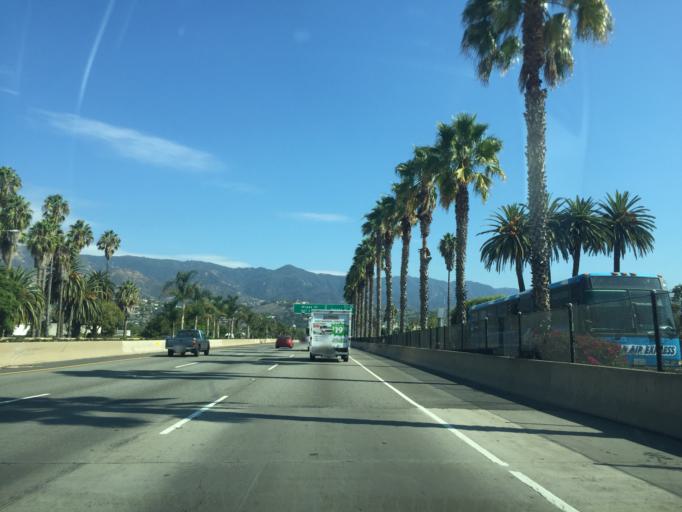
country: US
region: California
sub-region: Santa Barbara County
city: Santa Barbara
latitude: 34.4151
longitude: -119.6931
